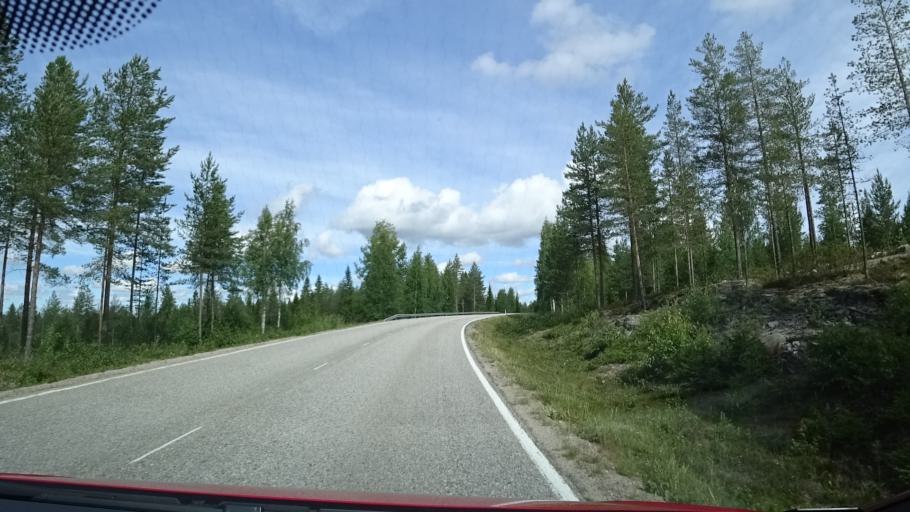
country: FI
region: Kainuu
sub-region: Kehys-Kainuu
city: Kuhmo
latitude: 64.4346
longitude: 29.8085
